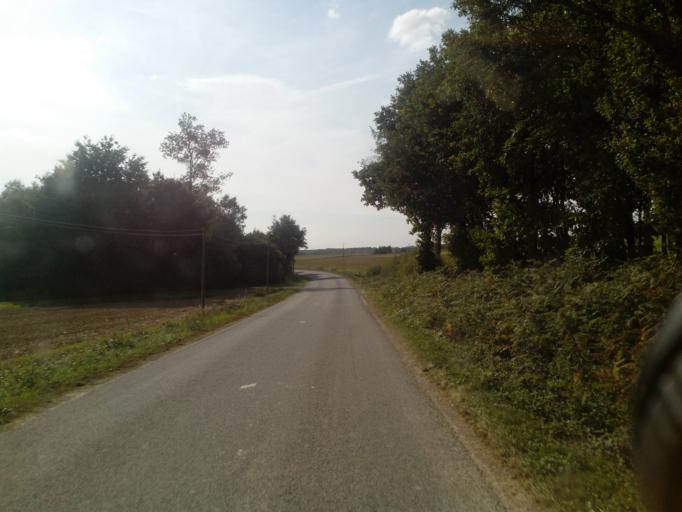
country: FR
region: Brittany
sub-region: Departement du Morbihan
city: Mauron
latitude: 48.1100
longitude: -2.3265
